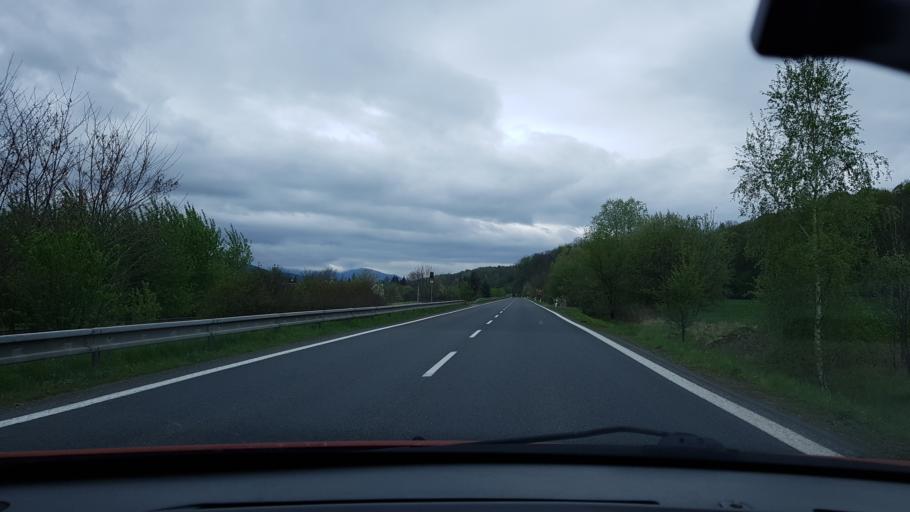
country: CZ
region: Olomoucky
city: Mikulovice
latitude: 50.3072
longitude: 17.3318
